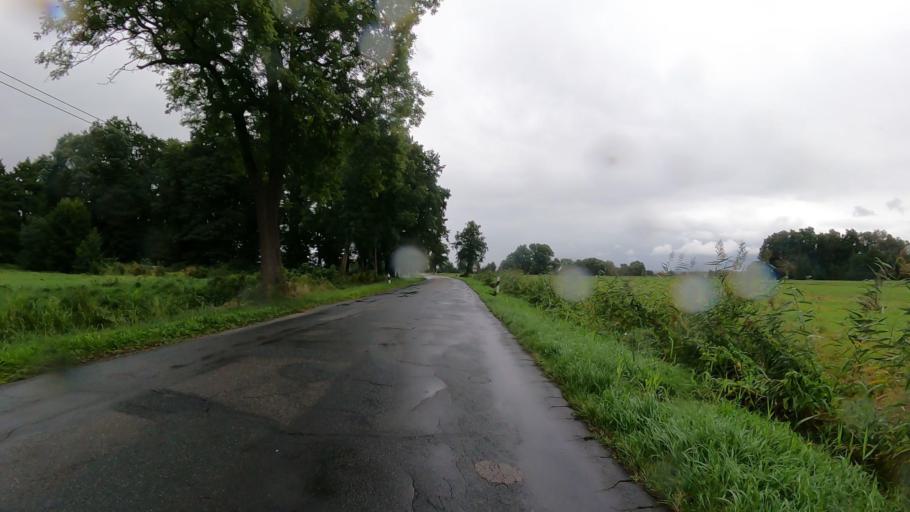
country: DE
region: Lower Saxony
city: Buxtehude
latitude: 53.4830
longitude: 9.7409
